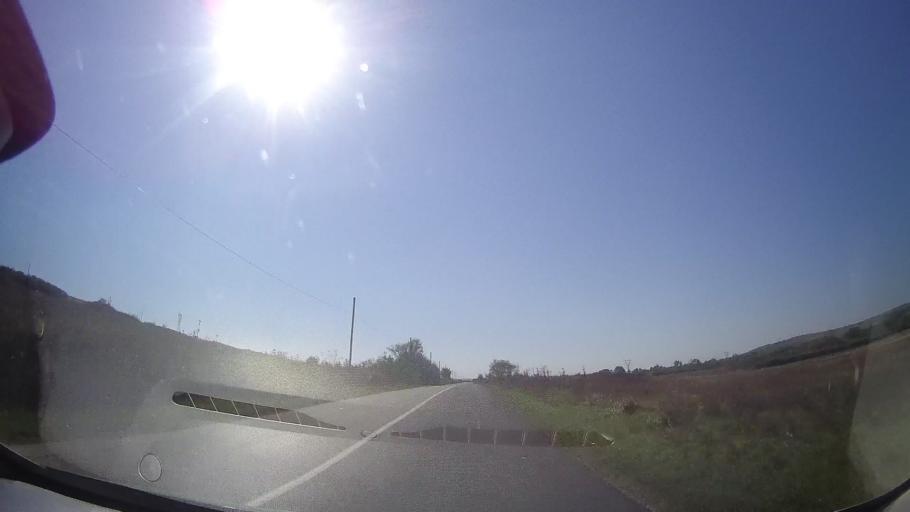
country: RO
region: Timis
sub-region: Comuna Bethausen
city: Bethausen
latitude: 45.8489
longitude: 21.9634
